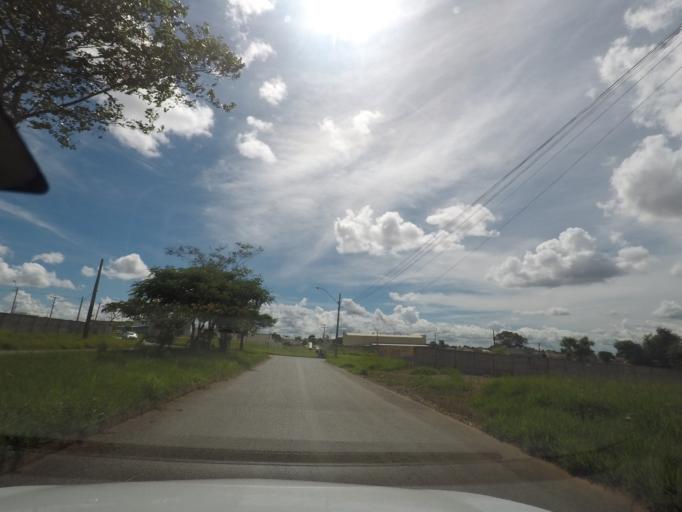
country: BR
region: Goias
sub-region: Goiania
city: Goiania
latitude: -16.7445
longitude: -49.3340
